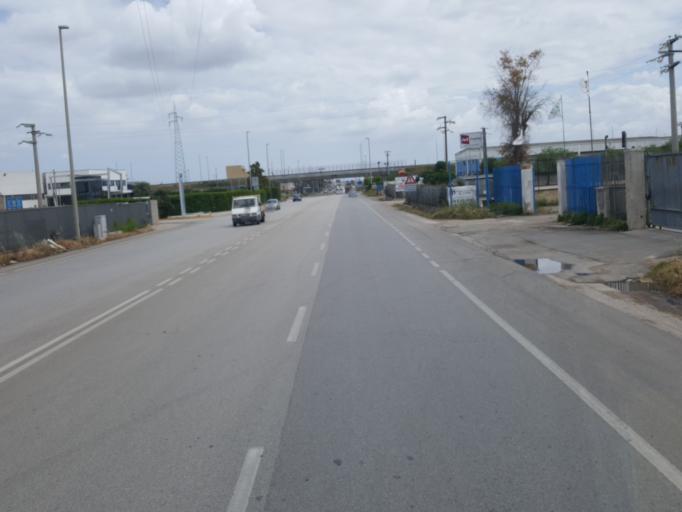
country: IT
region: Apulia
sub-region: Provincia di Bari
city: Modugno
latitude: 41.0926
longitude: 16.7545
